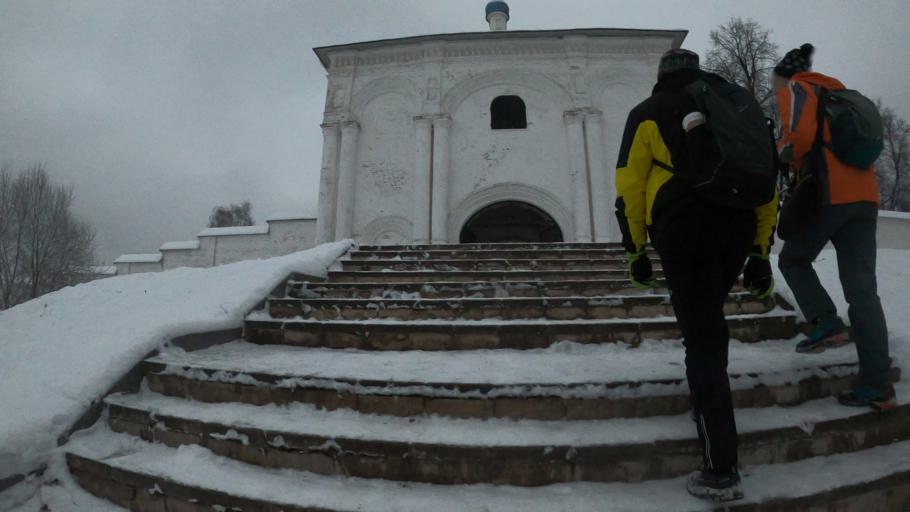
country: RU
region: Jaroslavl
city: Pereslavl'-Zalesskiy
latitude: 56.7207
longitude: 38.8370
